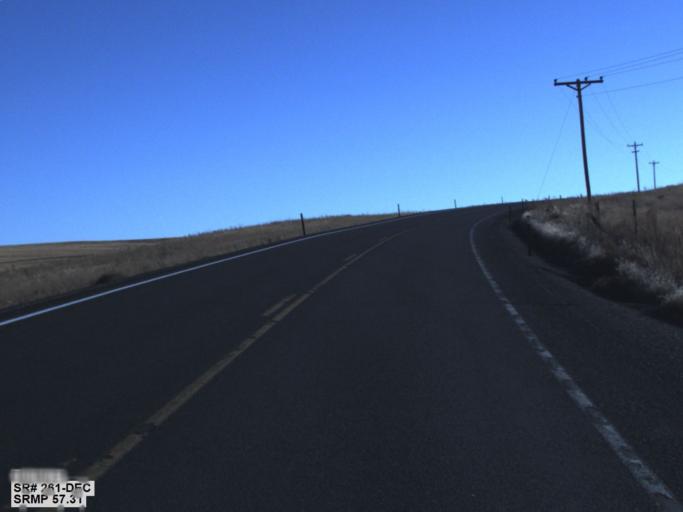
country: US
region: Washington
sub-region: Adams County
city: Ritzville
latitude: 47.0406
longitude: -118.3478
